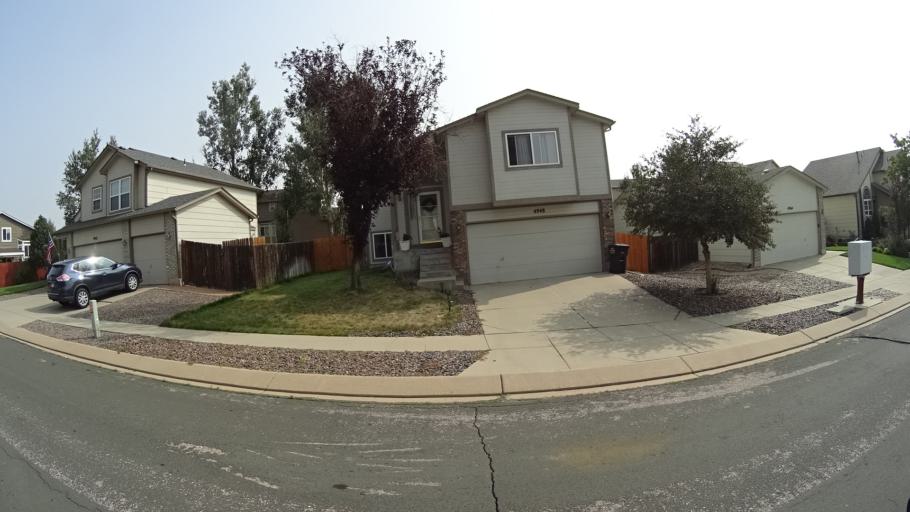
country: US
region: Colorado
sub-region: El Paso County
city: Cimarron Hills
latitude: 38.9279
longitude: -104.7329
